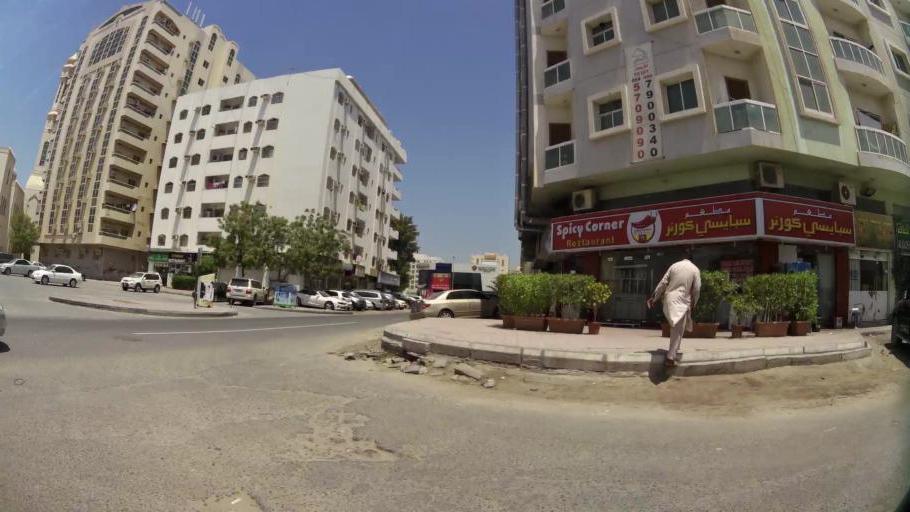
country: AE
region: Ajman
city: Ajman
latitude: 25.4011
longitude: 55.4454
